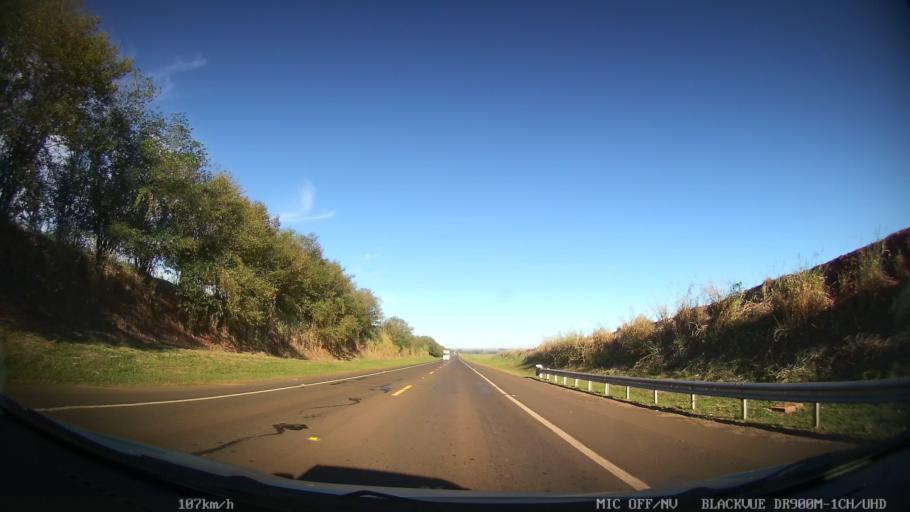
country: BR
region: Sao Paulo
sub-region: Americo Brasiliense
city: Americo Brasiliense
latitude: -21.7647
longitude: -48.1120
